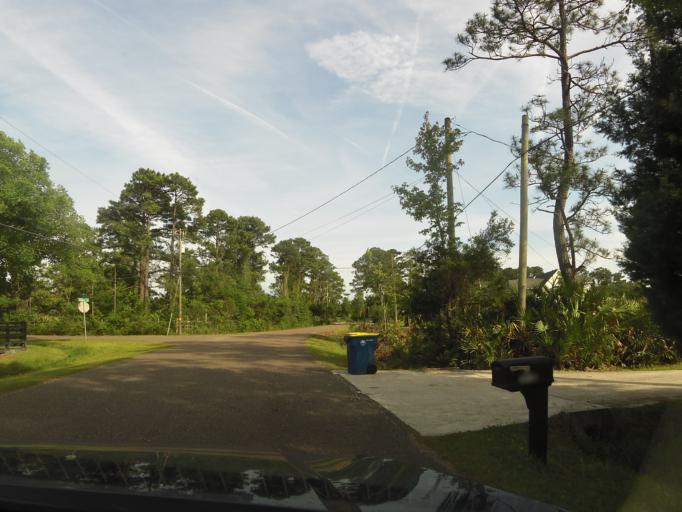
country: US
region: Florida
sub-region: Nassau County
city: Fernandina Beach
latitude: 30.5157
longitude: -81.4859
